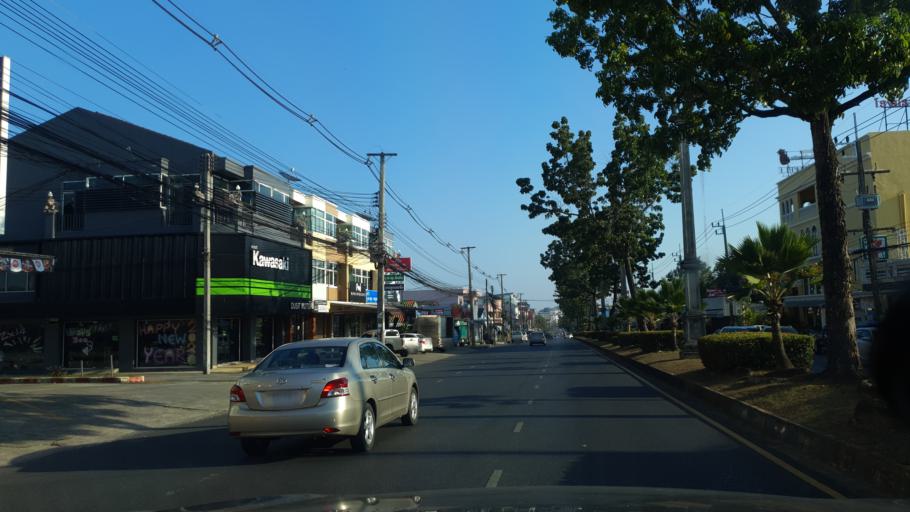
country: TH
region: Krabi
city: Krabi
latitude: 8.0757
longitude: 98.9098
